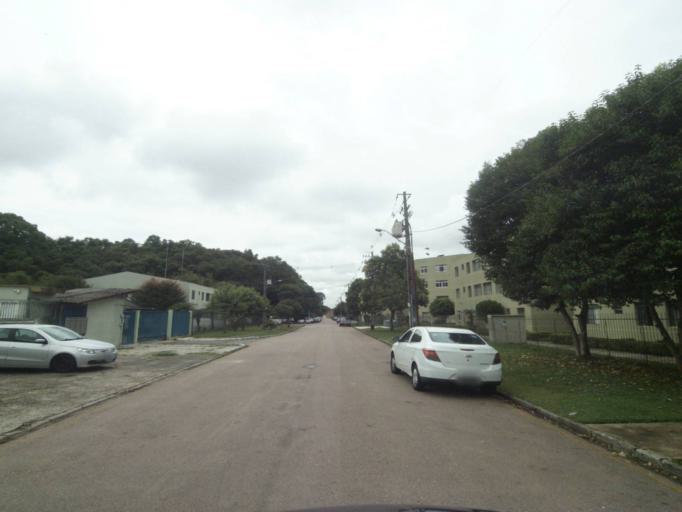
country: BR
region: Parana
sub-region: Curitiba
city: Curitiba
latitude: -25.4743
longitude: -49.3341
